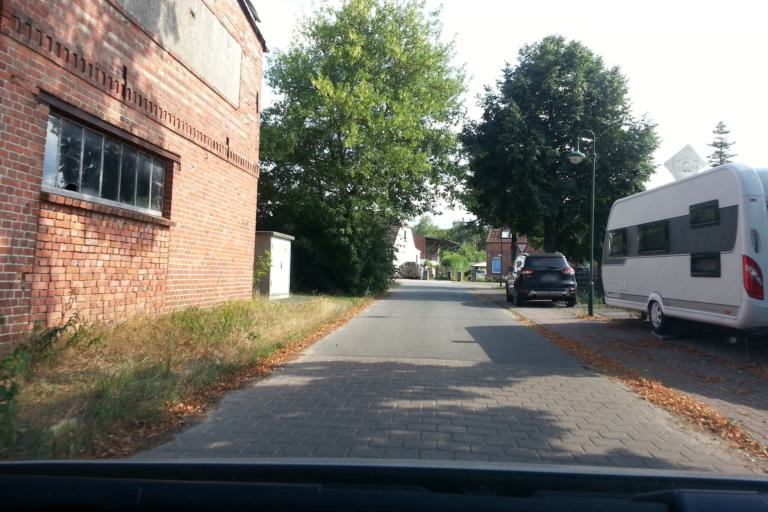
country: DE
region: Mecklenburg-Vorpommern
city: Ferdinandshof
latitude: 53.6341
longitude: 13.8505
